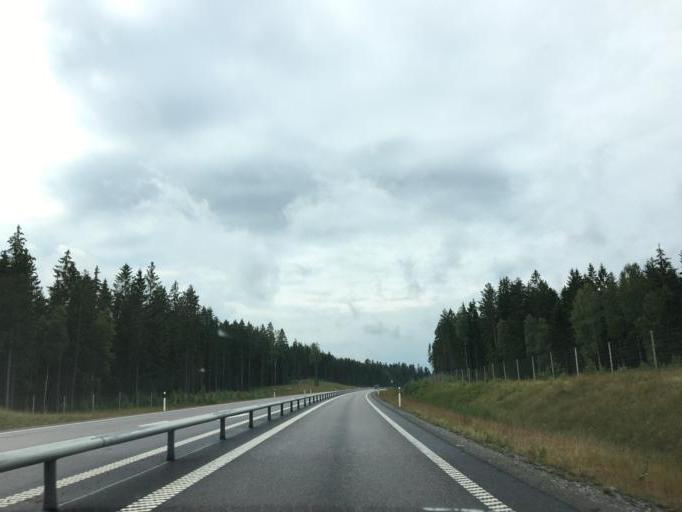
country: SE
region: Soedermanland
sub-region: Katrineholms Kommun
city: Katrineholm
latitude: 58.9805
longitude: 16.2664
